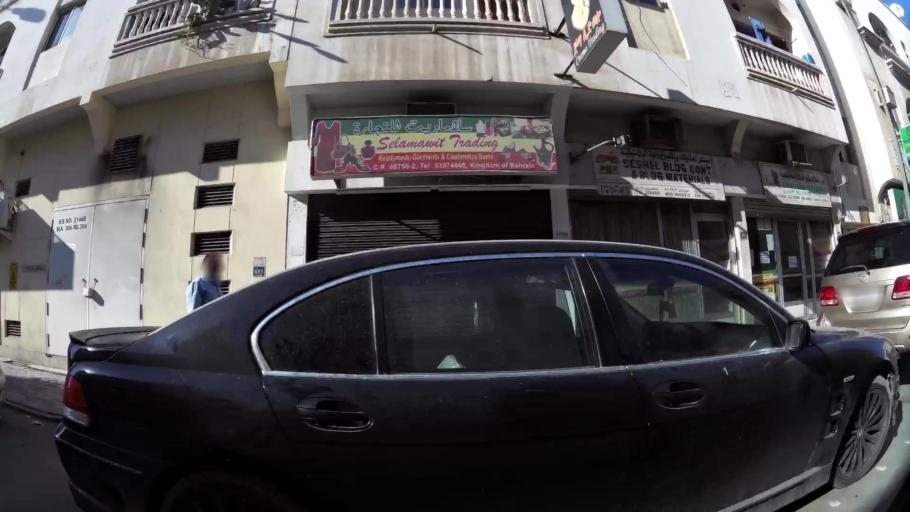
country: BH
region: Manama
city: Manama
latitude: 26.2315
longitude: 50.5873
